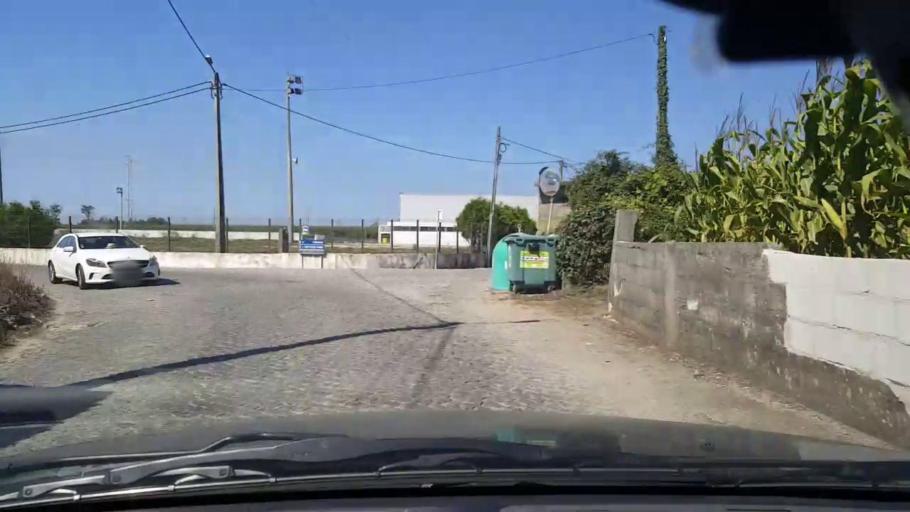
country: PT
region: Porto
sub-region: Matosinhos
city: Lavra
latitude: 41.2794
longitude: -8.7132
